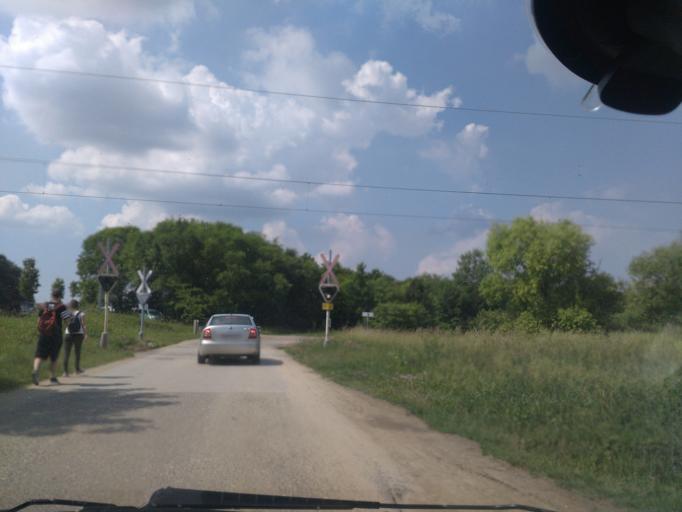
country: HU
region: Pest
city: Veresegyhaz
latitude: 47.6381
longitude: 19.2608
